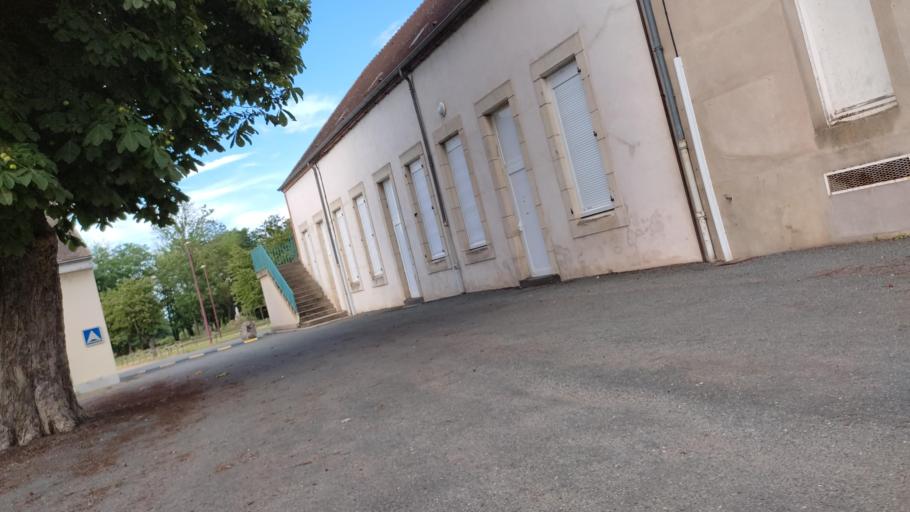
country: FR
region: Auvergne
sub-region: Departement de l'Allier
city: Beaulon
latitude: 46.6022
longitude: 3.6725
